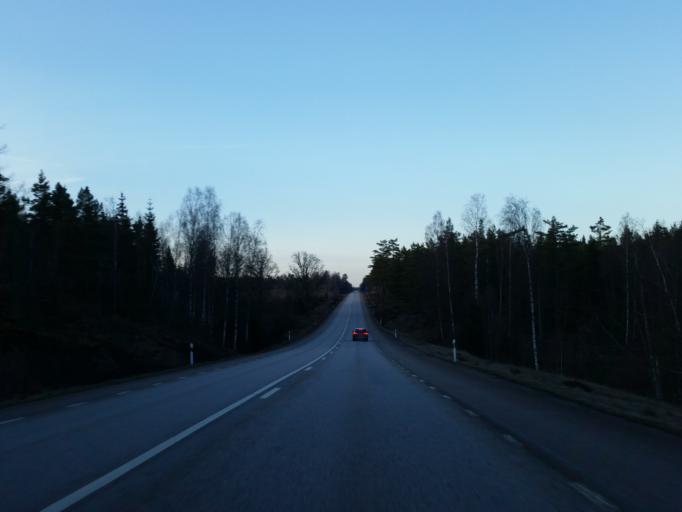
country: SE
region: Kalmar
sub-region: Oskarshamns Kommun
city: Oskarshamn
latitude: 57.4655
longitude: 16.5170
